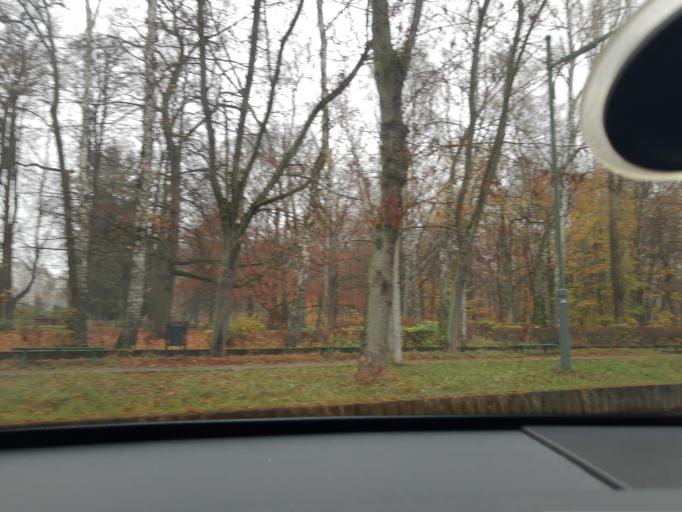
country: PL
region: Lodz Voivodeship
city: Lodz
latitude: 51.7634
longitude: 19.4131
